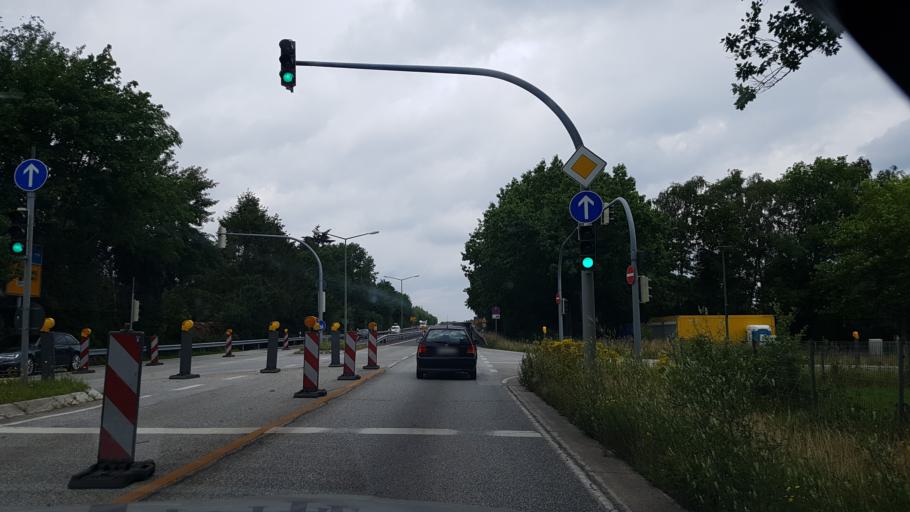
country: DE
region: Schleswig-Holstein
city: Neumunster
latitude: 54.0941
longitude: 9.9740
